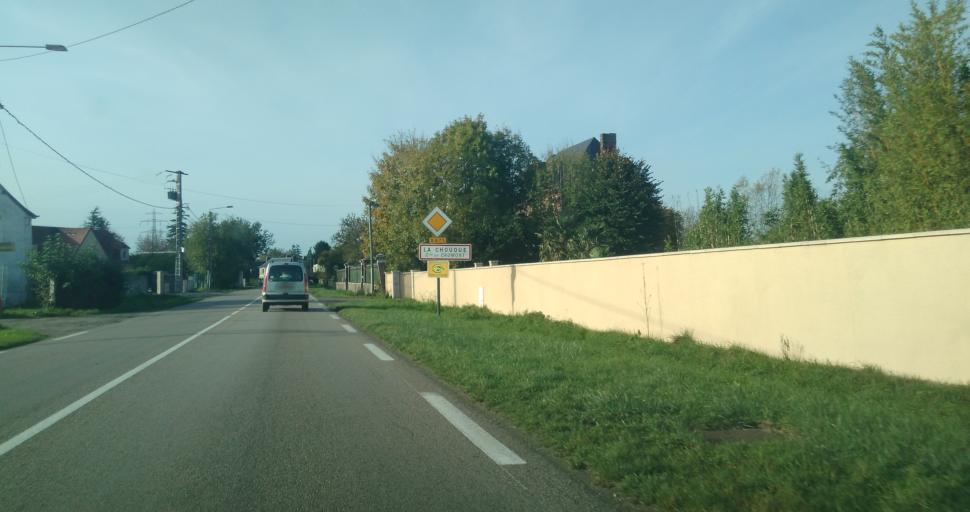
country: FR
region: Haute-Normandie
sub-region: Departement de l'Eure
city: Caumont
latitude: 49.3520
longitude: 0.9168
